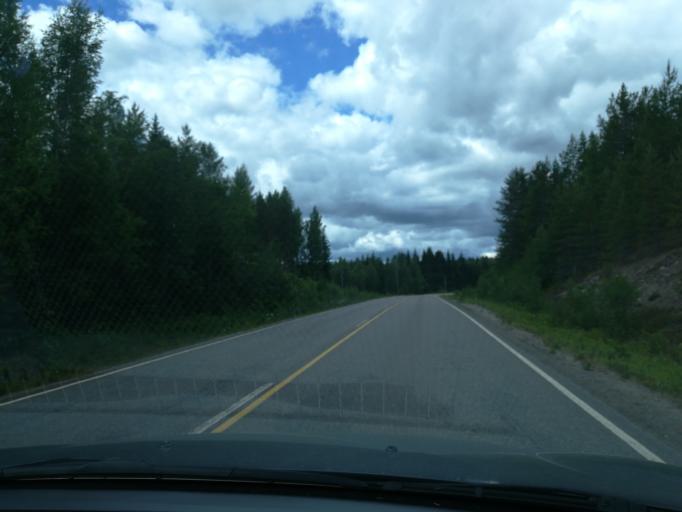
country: FI
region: Southern Savonia
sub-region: Mikkeli
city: Maentyharju
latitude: 61.3639
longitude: 27.0086
